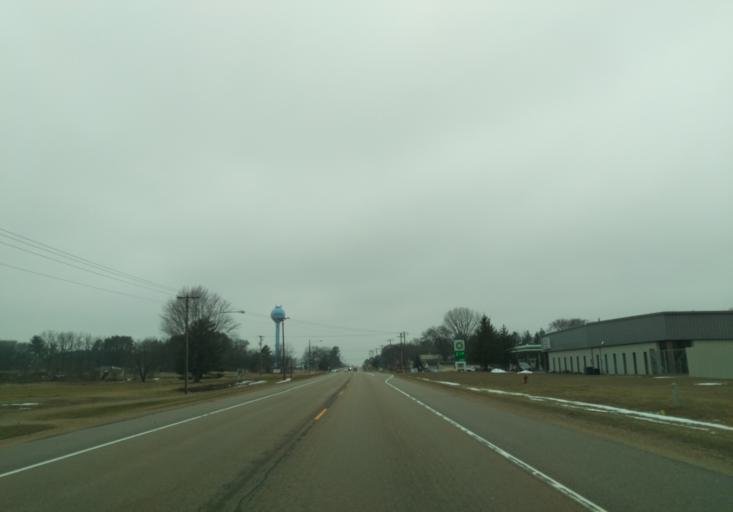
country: US
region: Wisconsin
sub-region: Dane County
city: Mazomanie
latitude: 43.1617
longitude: -89.9000
